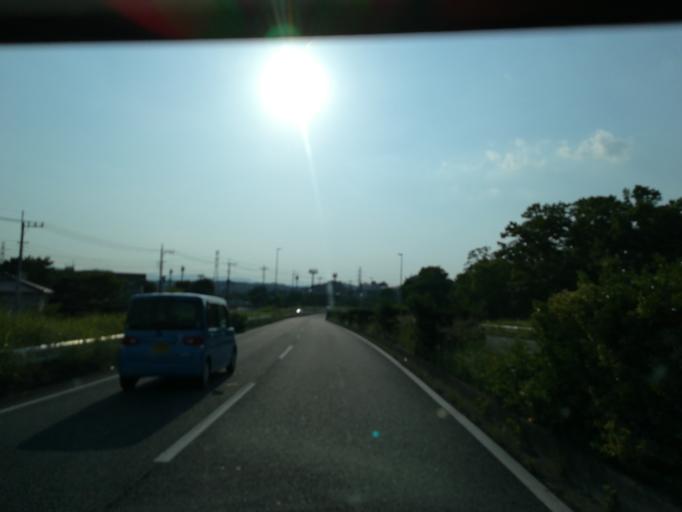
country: JP
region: Saitama
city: Kumagaya
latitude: 36.0666
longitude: 139.3654
